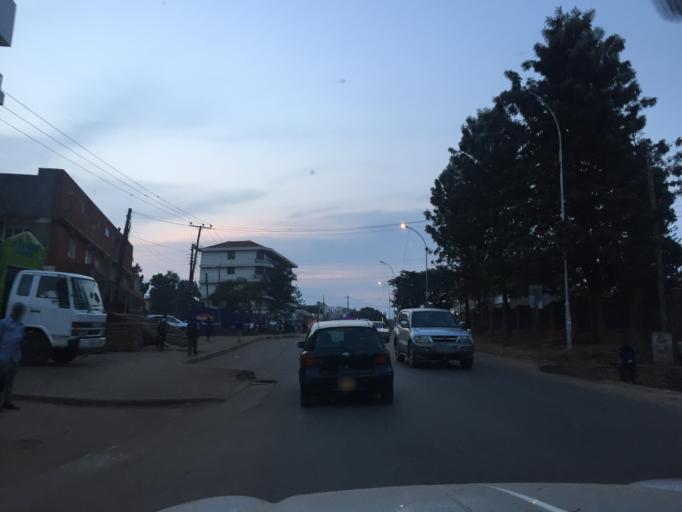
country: UG
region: Central Region
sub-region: Kampala District
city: Kampala
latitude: 0.2839
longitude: 32.6095
